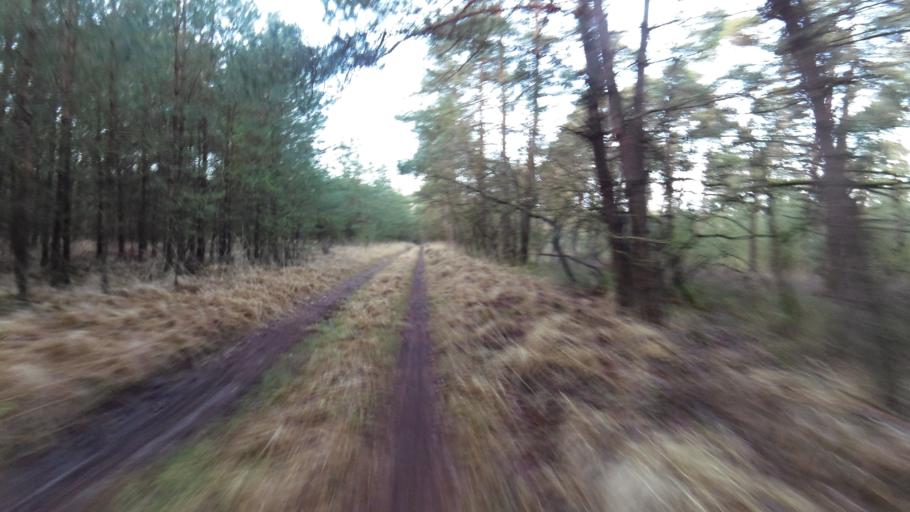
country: NL
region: Gelderland
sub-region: Gemeente Apeldoorn
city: Uddel
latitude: 52.2983
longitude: 5.8420
